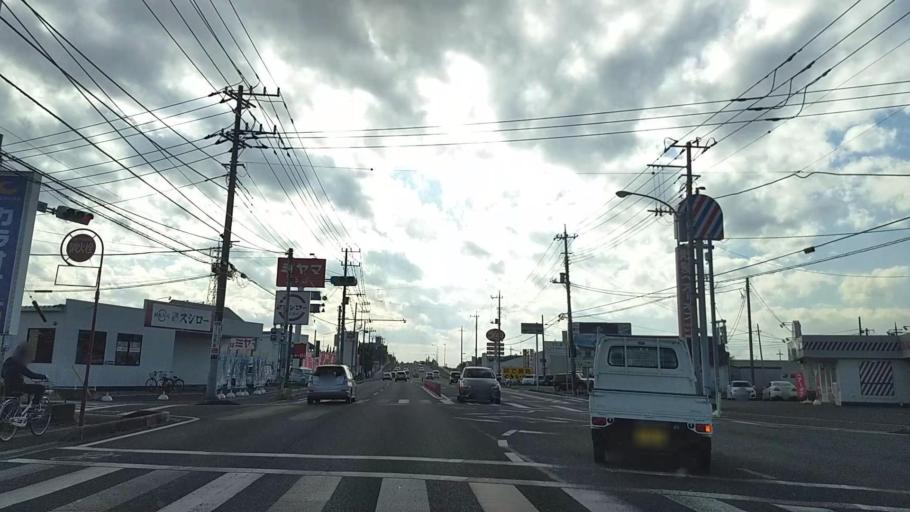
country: JP
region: Chiba
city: Togane
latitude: 35.5697
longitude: 140.3779
